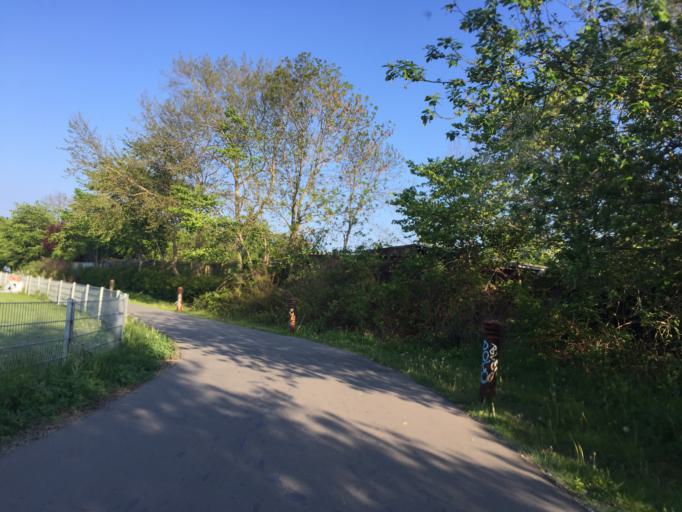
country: DK
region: Capital Region
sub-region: Kobenhavn
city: Christianshavn
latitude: 55.6701
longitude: 12.6077
